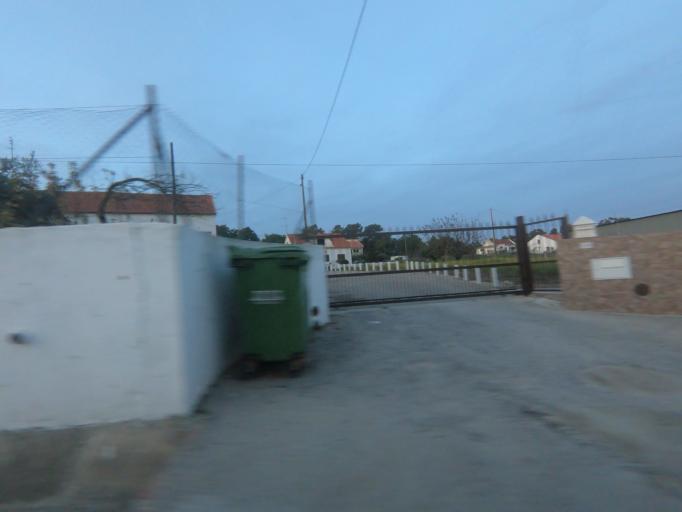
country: PT
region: Setubal
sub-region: Setubal
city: Setubal
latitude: 38.5236
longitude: -8.8371
